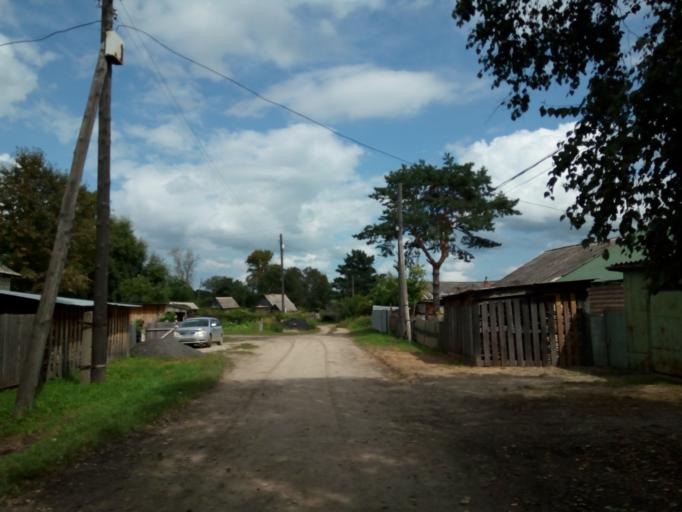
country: RU
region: Primorskiy
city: Dal'nerechensk
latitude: 45.9528
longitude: 133.8097
